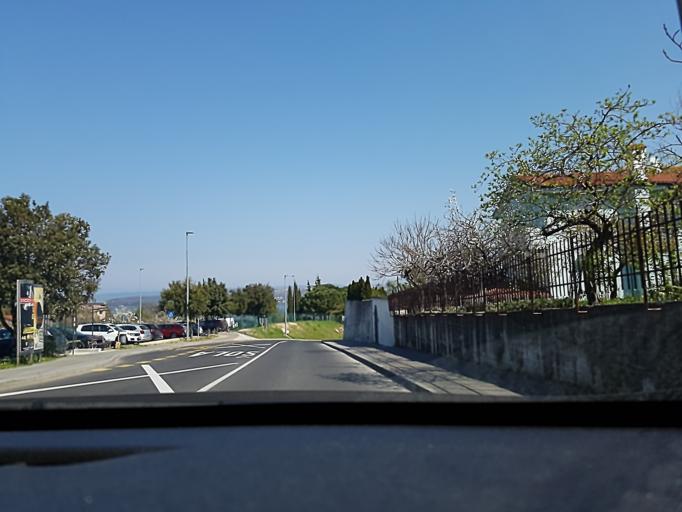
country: SI
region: Koper-Capodistria
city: Koper
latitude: 45.5427
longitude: 13.7123
